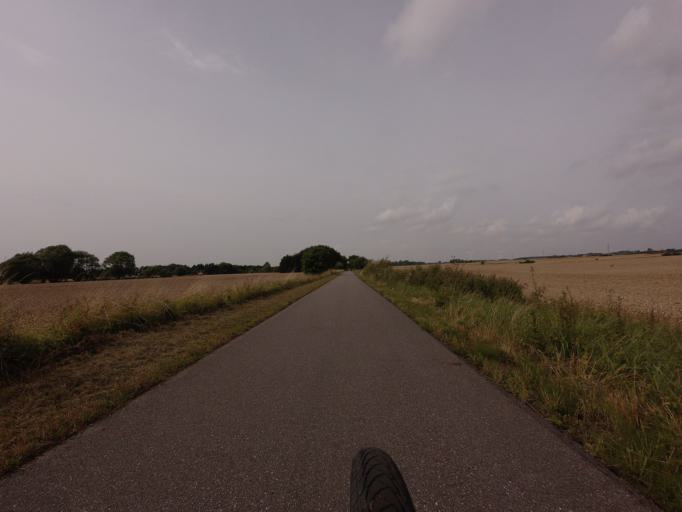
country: DK
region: Zealand
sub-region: Naestved Kommune
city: Naestved
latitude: 55.2565
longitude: 11.6547
